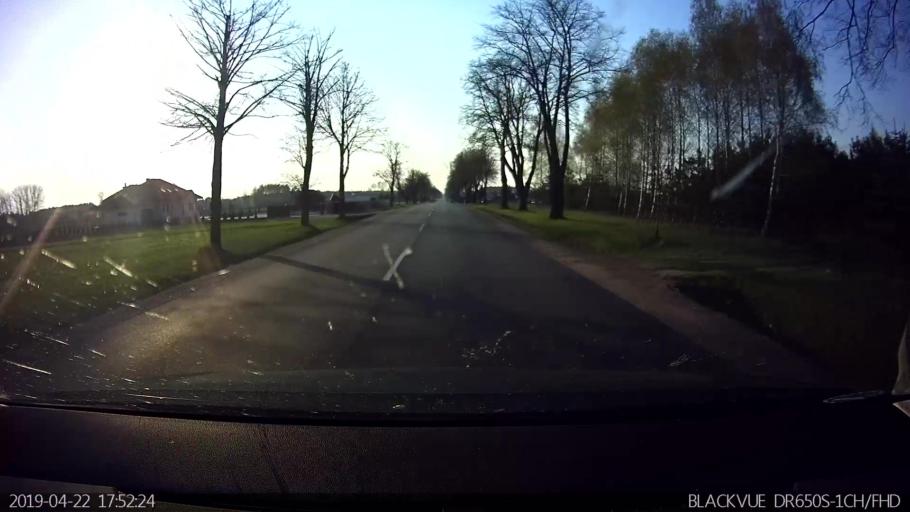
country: PL
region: Masovian Voivodeship
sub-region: Powiat wegrowski
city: Wegrow
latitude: 52.4426
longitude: 21.9770
